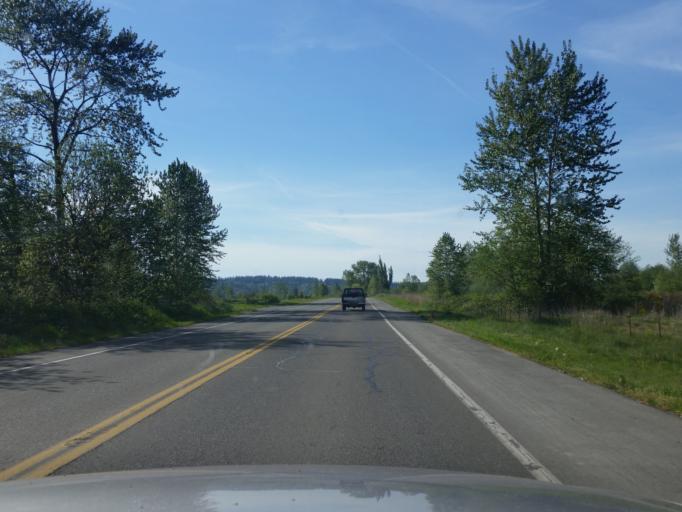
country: US
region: Washington
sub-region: Snohomish County
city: Fobes Hill
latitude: 47.9216
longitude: -122.1513
